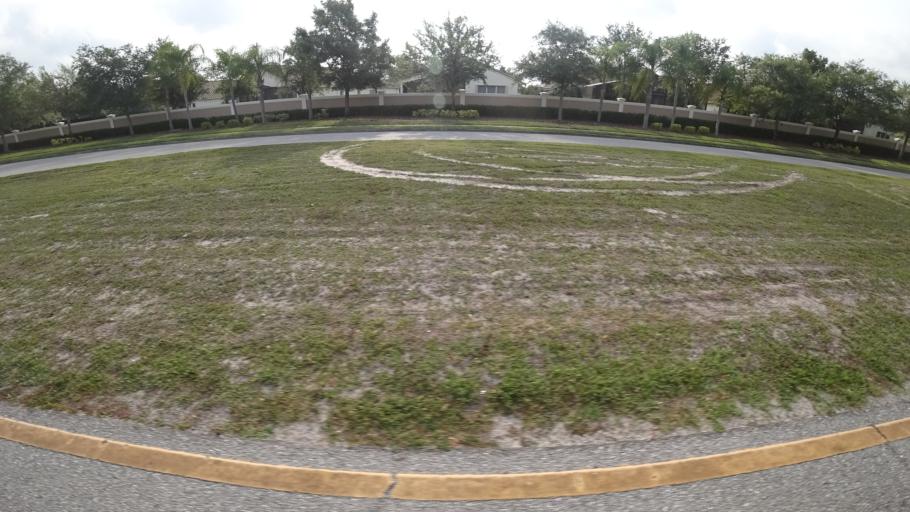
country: US
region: Florida
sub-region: Sarasota County
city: North Sarasota
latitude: 27.4223
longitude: -82.5128
